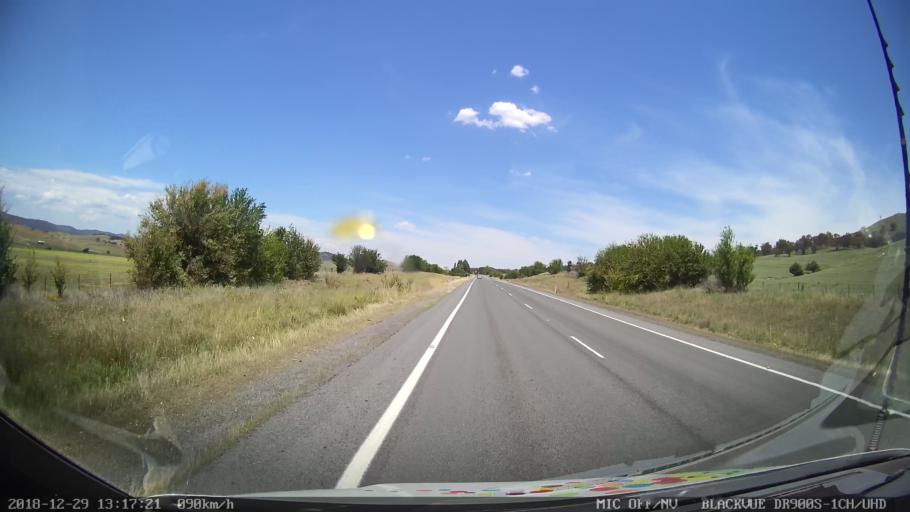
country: AU
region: Australian Capital Territory
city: Macarthur
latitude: -35.7363
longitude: 149.1607
